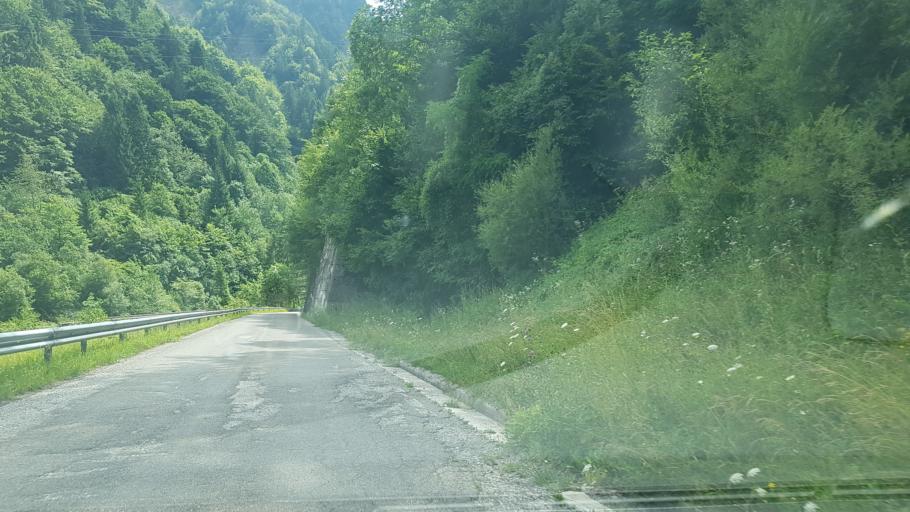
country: IT
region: Friuli Venezia Giulia
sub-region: Provincia di Udine
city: Moggio Udinese
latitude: 46.4921
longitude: 13.2007
